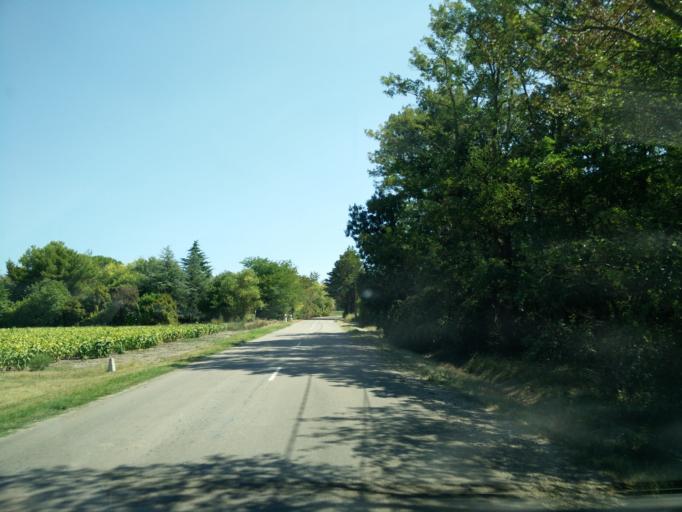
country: FR
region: Rhone-Alpes
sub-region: Departement de la Drome
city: Montboucher-sur-Jabron
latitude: 44.5484
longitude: 4.8342
